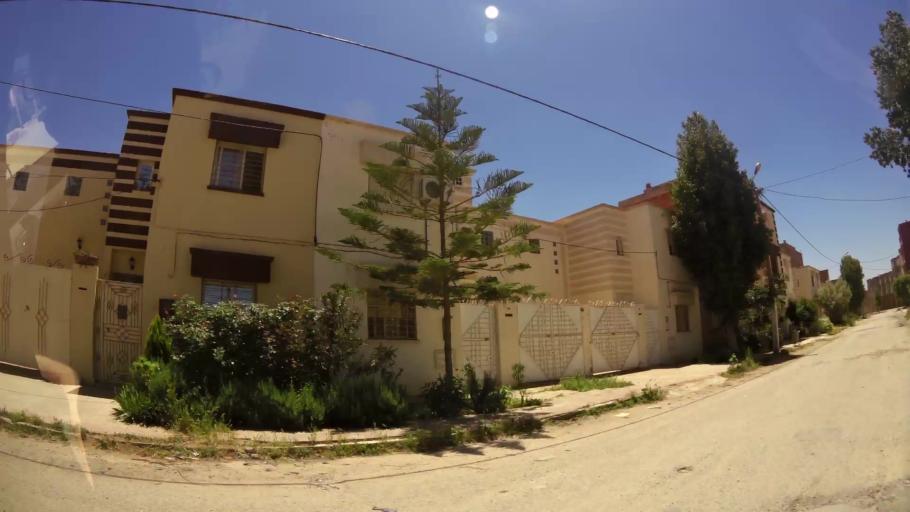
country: MA
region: Oriental
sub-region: Oujda-Angad
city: Oujda
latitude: 34.6787
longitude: -1.8715
